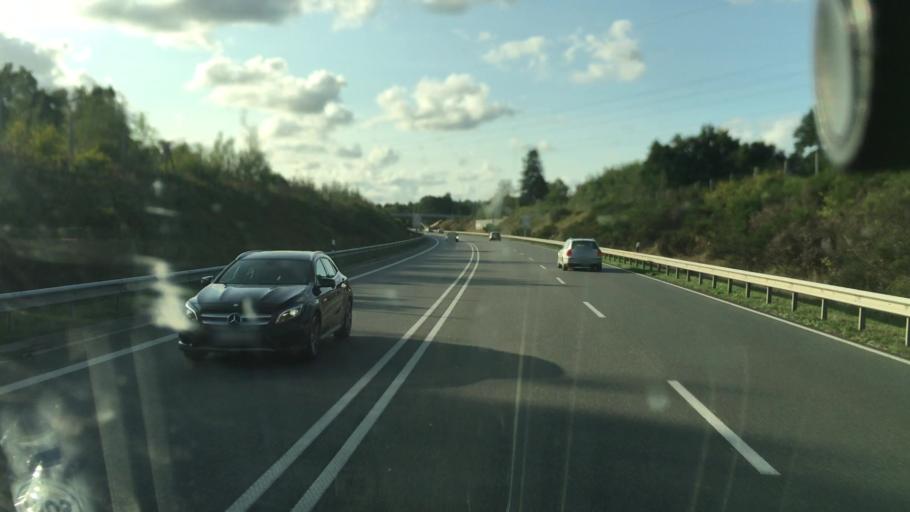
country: DE
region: Lower Saxony
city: Schortens
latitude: 53.5497
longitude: 7.9631
